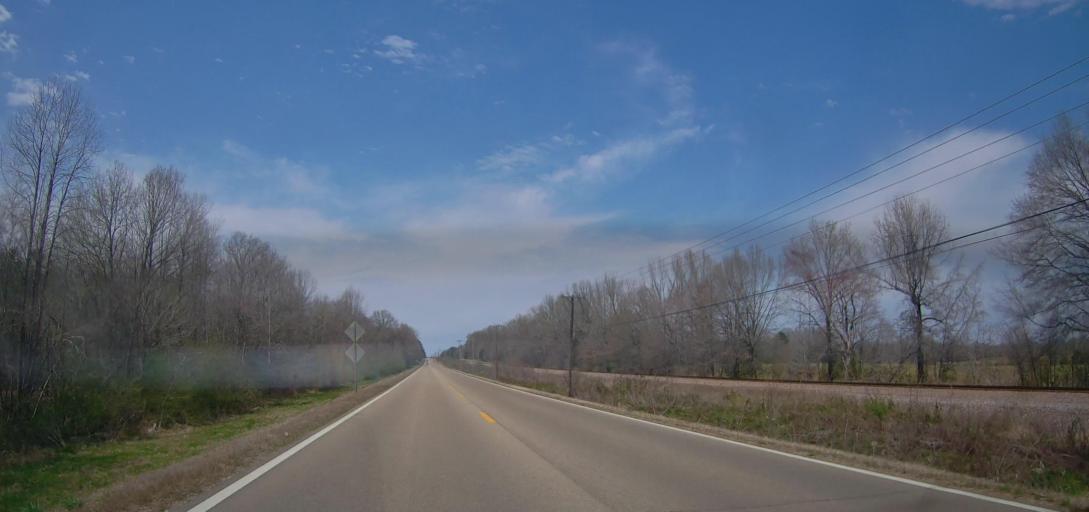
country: US
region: Mississippi
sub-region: Union County
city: New Albany
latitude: 34.5227
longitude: -89.0596
